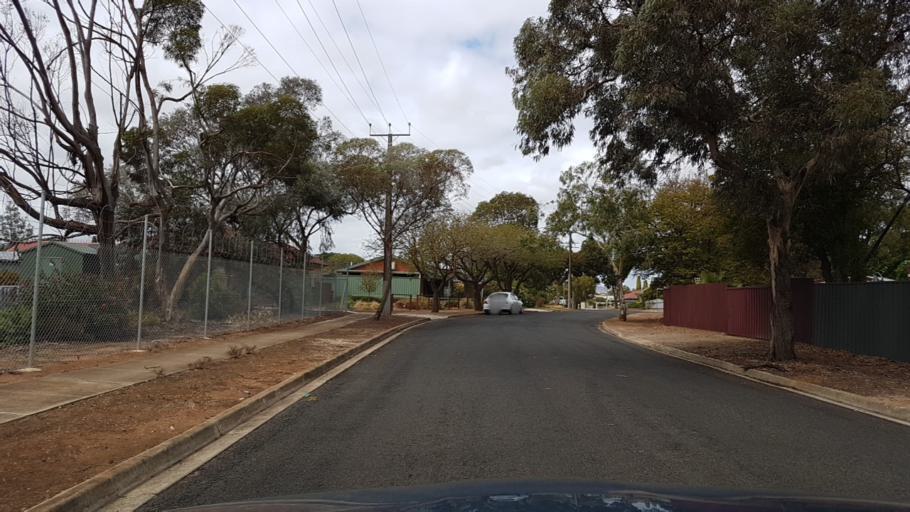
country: AU
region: South Australia
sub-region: Gawler
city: Gawler
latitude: -34.6031
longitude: 138.7605
